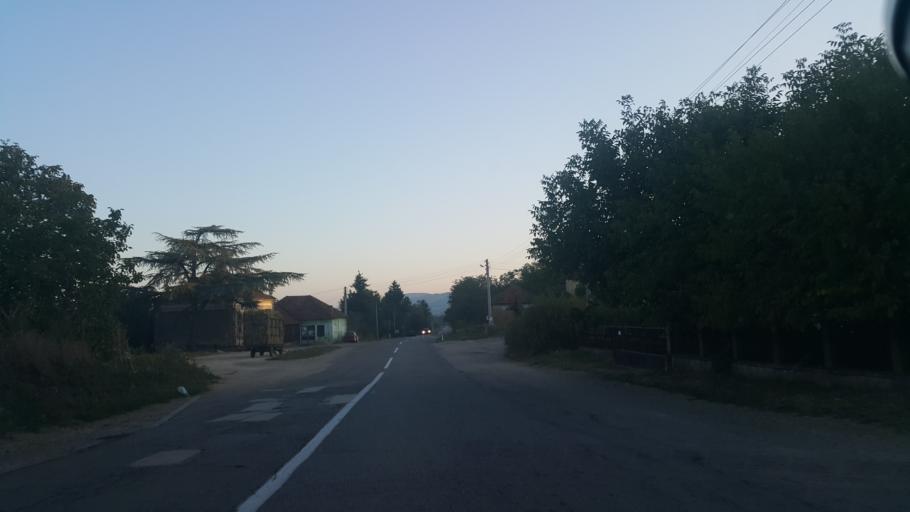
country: RS
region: Central Serbia
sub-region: Zajecarski Okrug
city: Knjazevac
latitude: 43.7275
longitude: 22.3094
